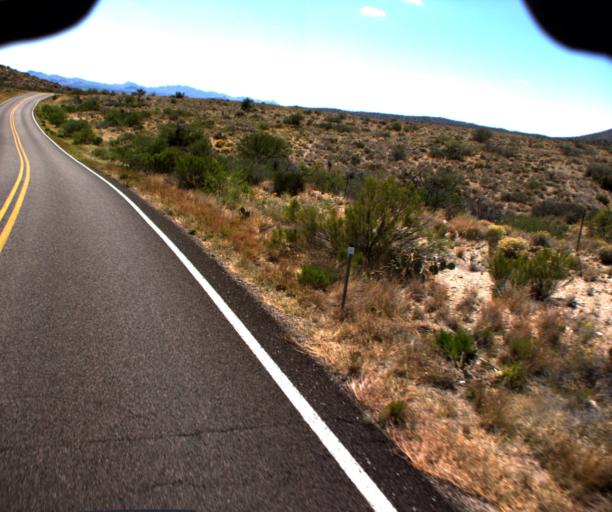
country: US
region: Arizona
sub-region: Yavapai County
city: Bagdad
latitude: 34.5044
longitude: -113.1574
